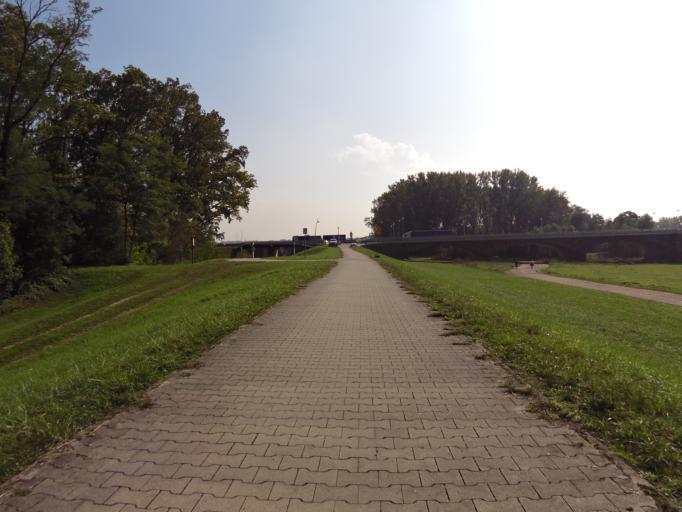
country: DE
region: Rheinland-Pfalz
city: Worms
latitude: 49.6337
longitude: 8.3856
